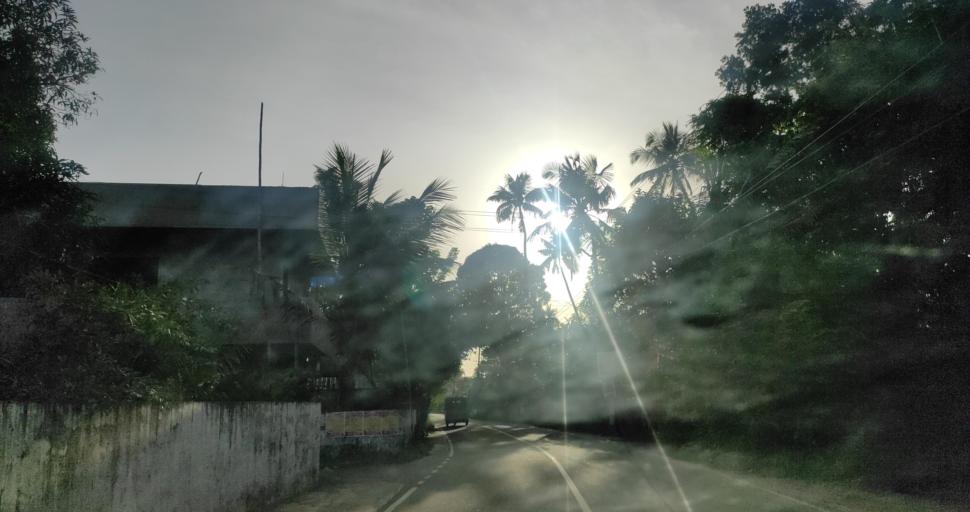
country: IN
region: Kerala
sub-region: Alappuzha
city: Shertallai
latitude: 9.6018
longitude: 76.3055
